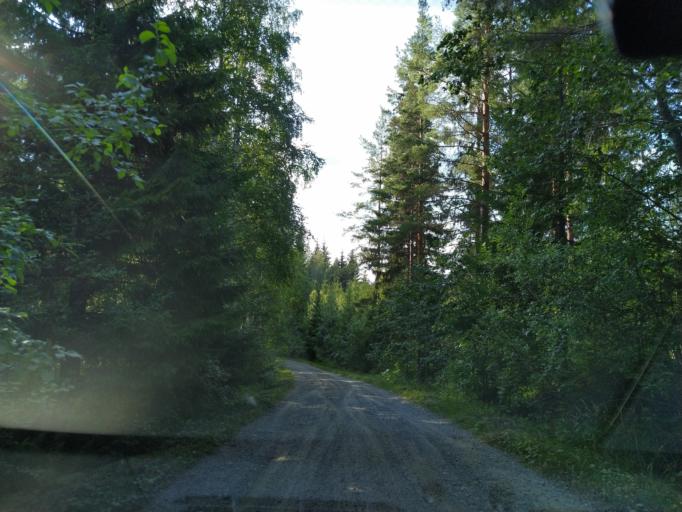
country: FI
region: Central Finland
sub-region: Jaemsae
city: Kuhmoinen
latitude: 61.7142
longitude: 24.9140
